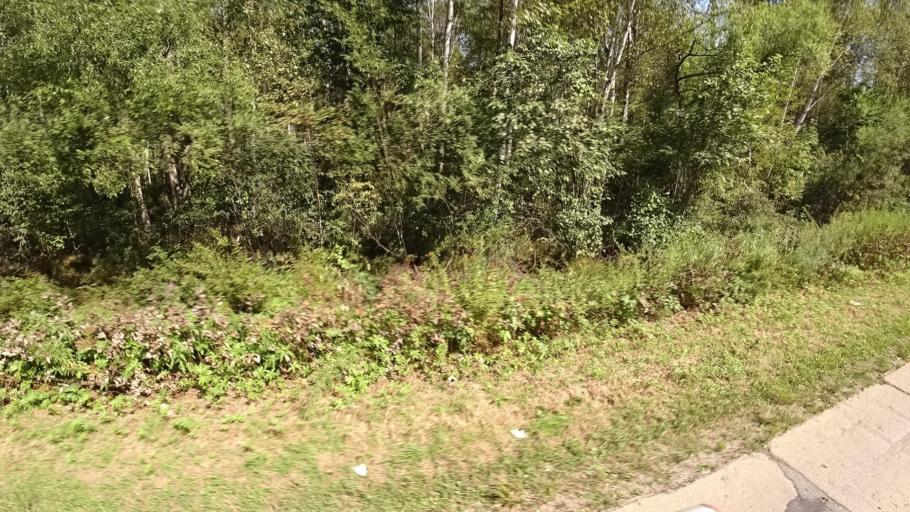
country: RU
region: Khabarovsk Krai
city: Khor
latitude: 47.9842
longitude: 135.0972
